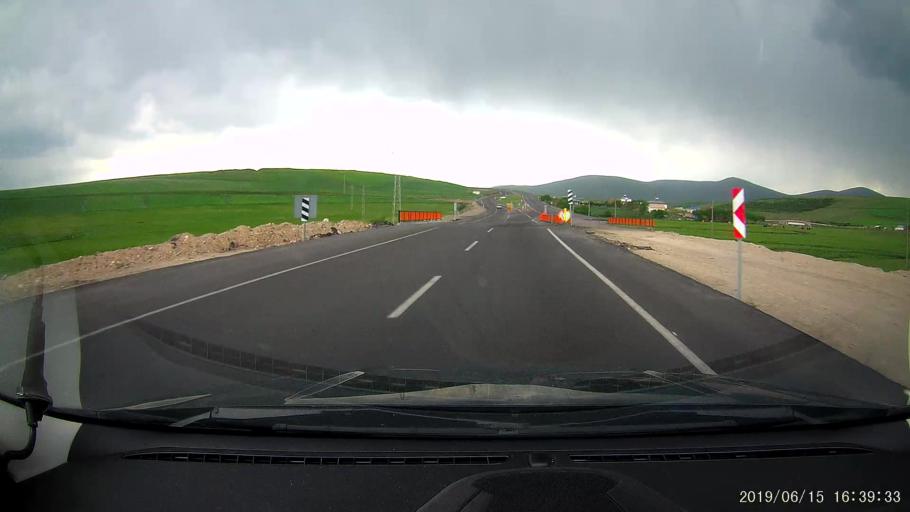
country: TR
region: Ardahan
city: Haskoy
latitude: 40.9817
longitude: 42.8968
